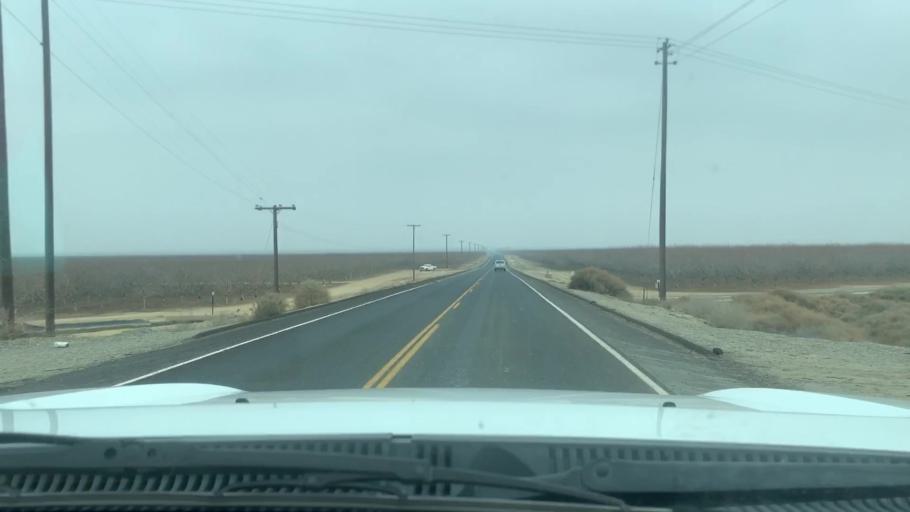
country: US
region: California
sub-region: Kern County
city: Lost Hills
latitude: 35.4993
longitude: -119.6468
